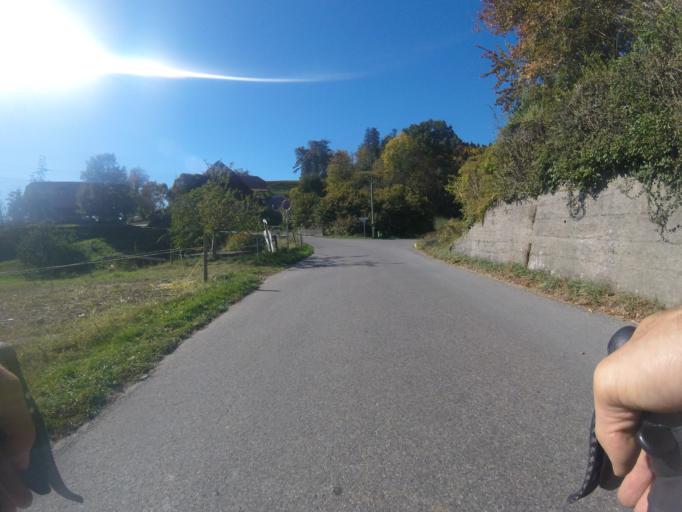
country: CH
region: Bern
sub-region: Bern-Mittelland District
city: Wohlen
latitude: 46.9678
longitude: 7.3513
